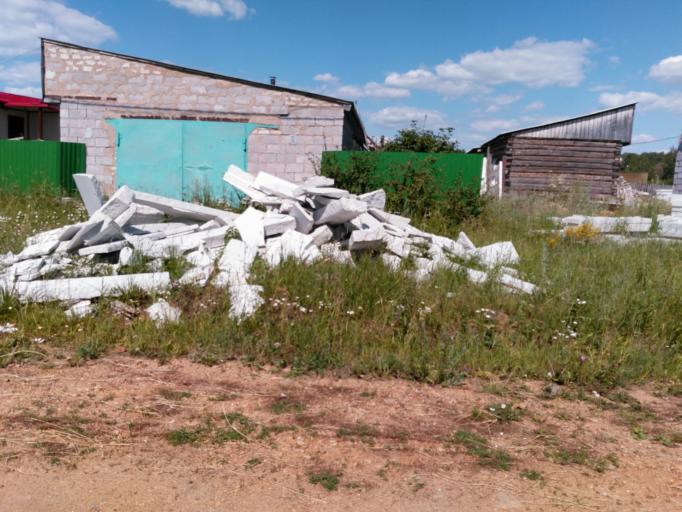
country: RU
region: Bashkortostan
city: Uchaly
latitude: 54.2892
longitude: 59.3640
